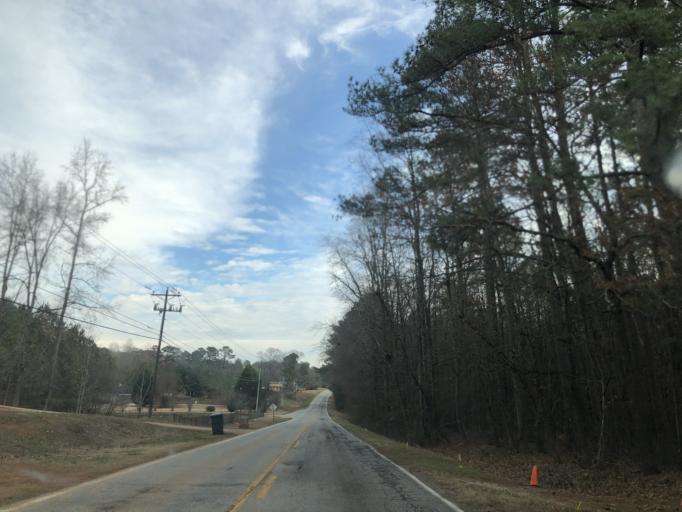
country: US
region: Georgia
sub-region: Henry County
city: Stockbridge
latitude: 33.6073
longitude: -84.2043
